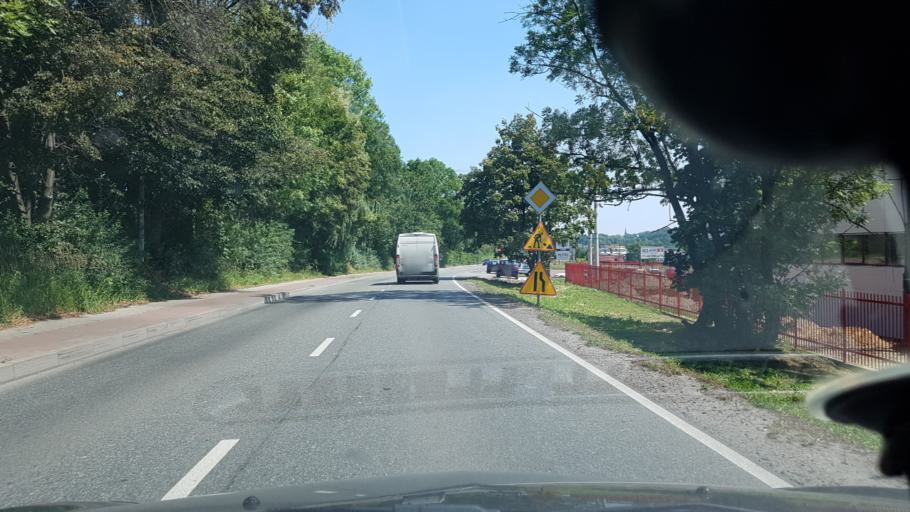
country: PL
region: Silesian Voivodeship
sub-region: Powiat wodzislawski
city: Wodzislaw Slaski
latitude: 50.0144
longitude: 18.4859
